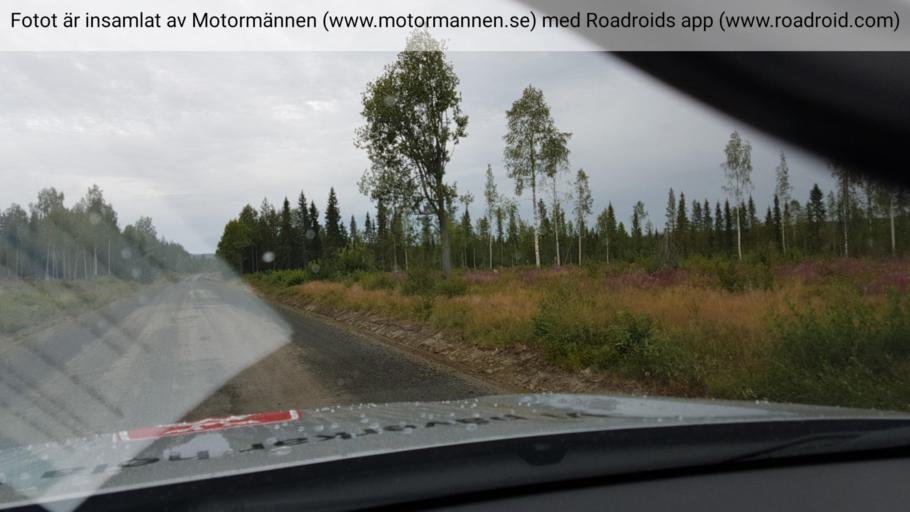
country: SE
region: Norrbotten
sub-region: Alvsbyns Kommun
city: AElvsbyn
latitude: 65.9223
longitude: 21.2636
